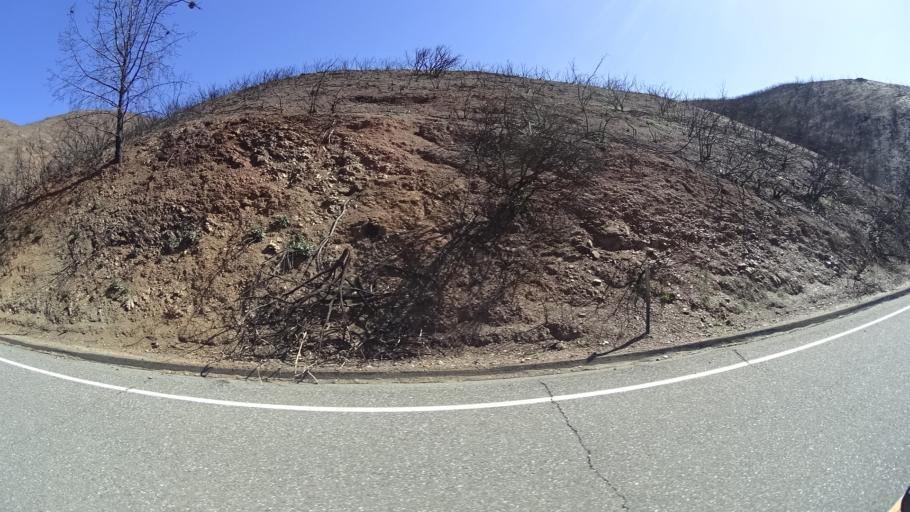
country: US
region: California
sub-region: Tehama County
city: Rancho Tehama Reserve
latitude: 39.6513
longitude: -122.6171
